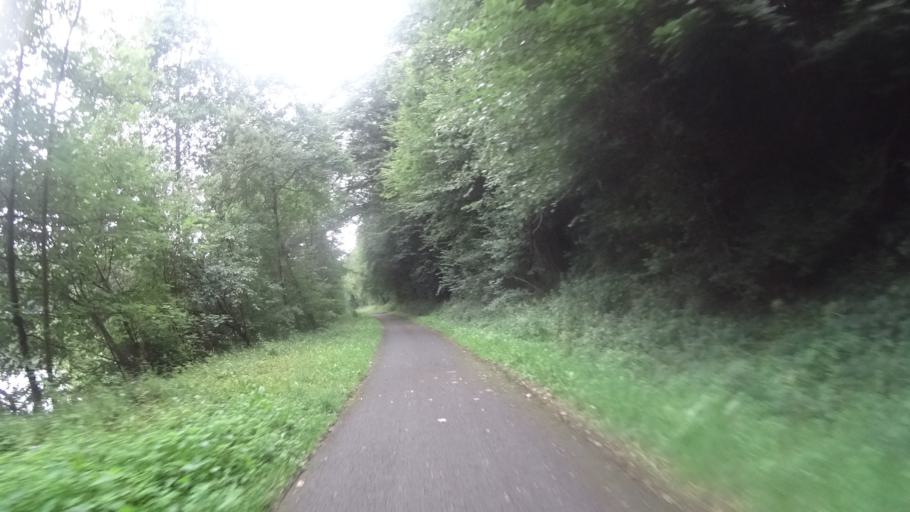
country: FR
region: Lorraine
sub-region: Departement de Meurthe-et-Moselle
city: Velaine-en-Haye
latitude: 48.6581
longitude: 6.0231
